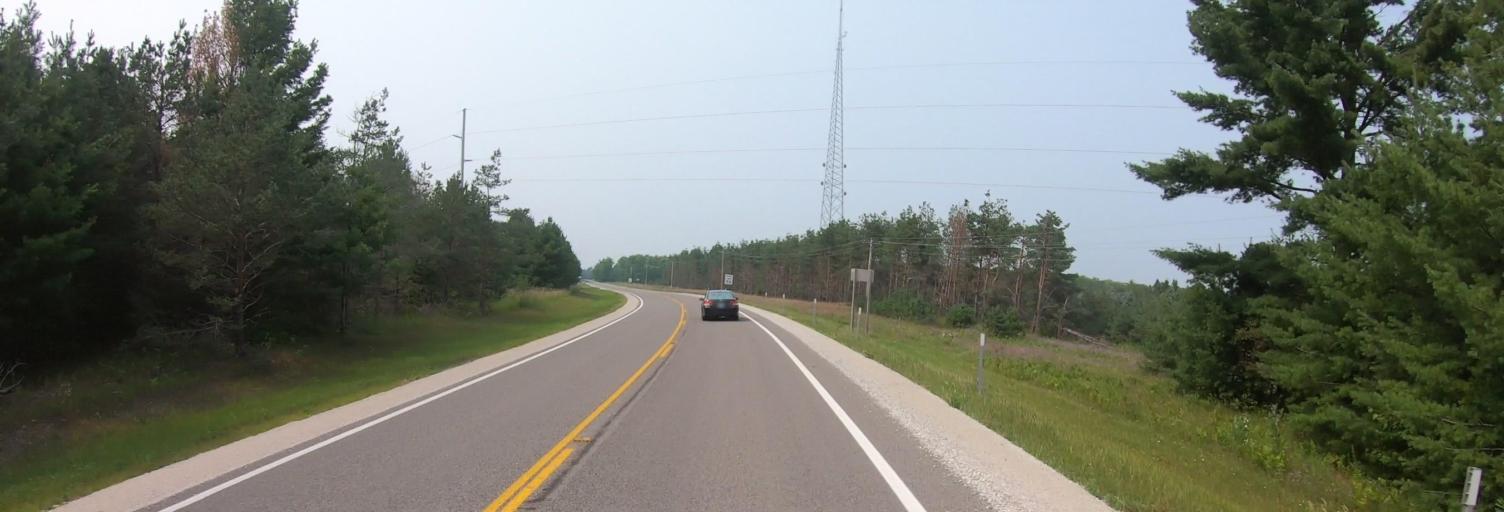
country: US
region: Michigan
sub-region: Chippewa County
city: Sault Ste. Marie
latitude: 46.0213
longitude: -84.0719
